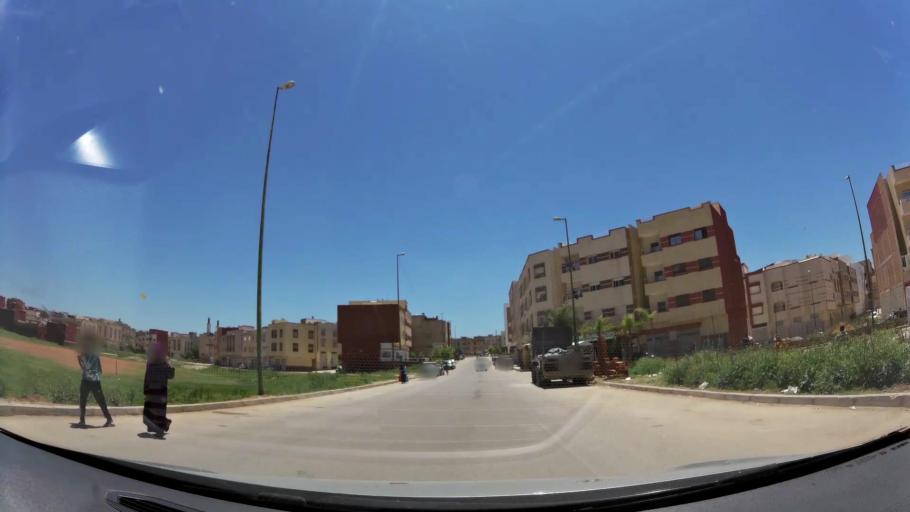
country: MA
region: Meknes-Tafilalet
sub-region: Meknes
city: Meknes
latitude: 33.8584
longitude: -5.5604
